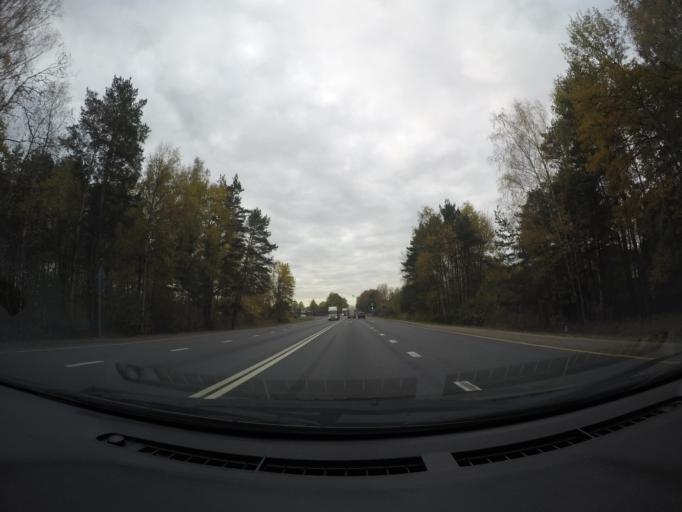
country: RU
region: Moskovskaya
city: Gzhel'
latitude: 55.6463
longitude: 38.3727
